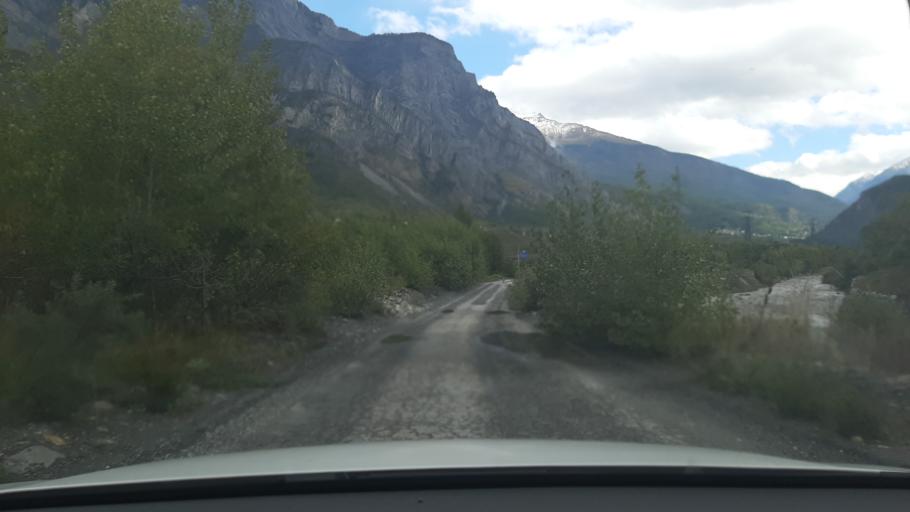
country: FR
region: Rhone-Alpes
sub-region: Departement de la Savoie
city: Villargondran
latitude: 45.2501
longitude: 6.4015
